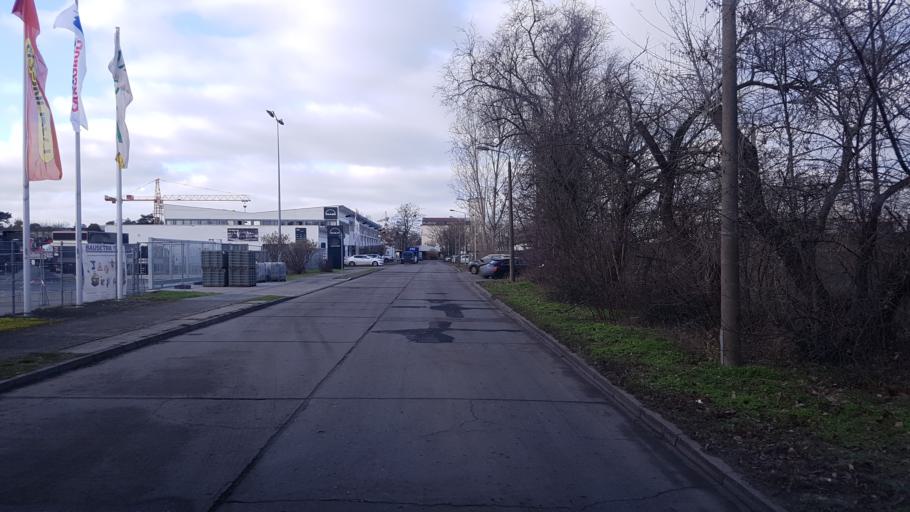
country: DE
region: Brandenburg
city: Potsdam
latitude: 52.3599
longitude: 13.1082
